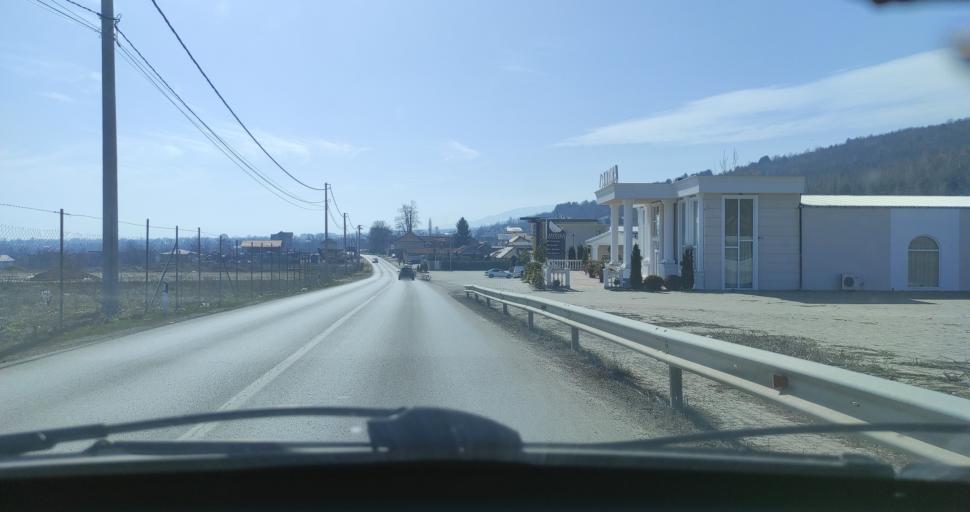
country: XK
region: Gjakova
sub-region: Komuna e Decanit
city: Strellc i Eperm
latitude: 42.5713
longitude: 20.2933
